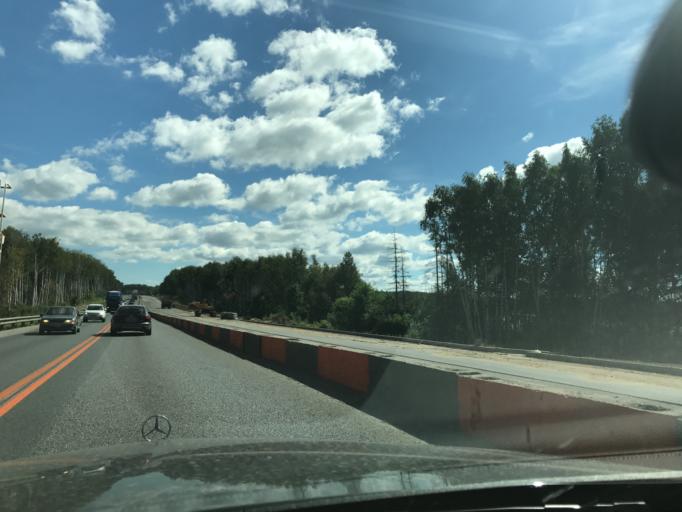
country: RU
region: Vladimir
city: Novovyazniki
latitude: 56.2091
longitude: 42.2732
